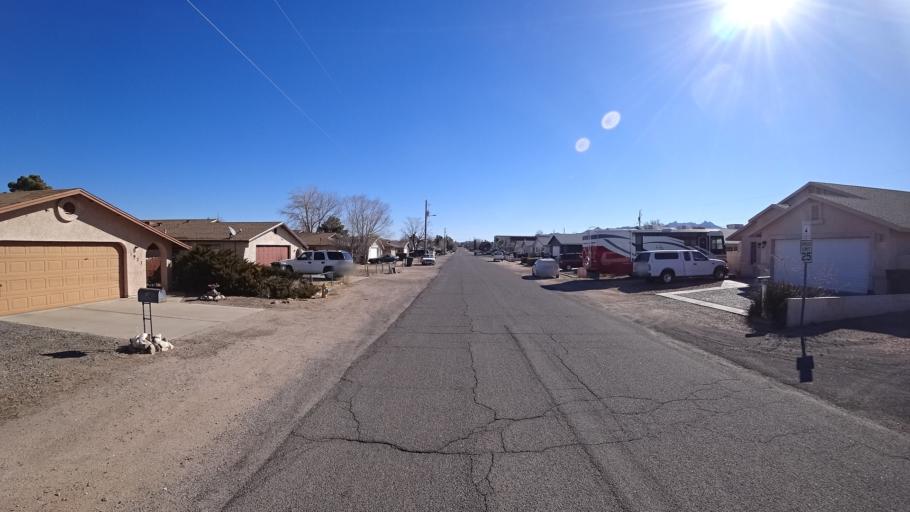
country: US
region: Arizona
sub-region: Mohave County
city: Kingman
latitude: 35.2039
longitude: -114.0328
